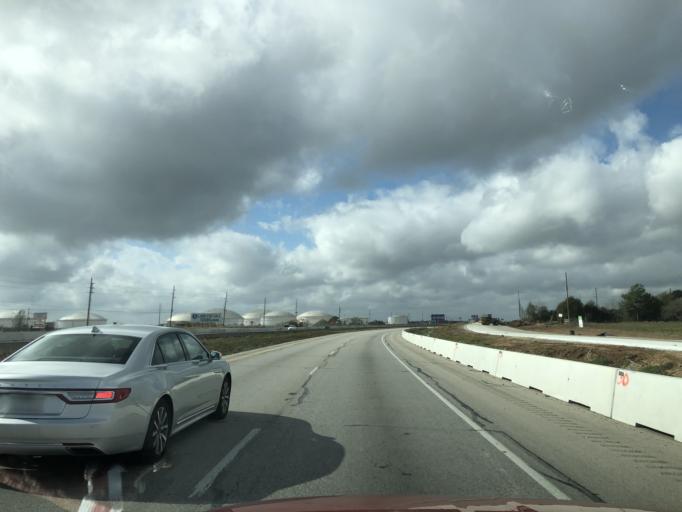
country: US
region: Texas
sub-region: Austin County
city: Sealy
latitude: 29.7694
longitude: -96.1403
